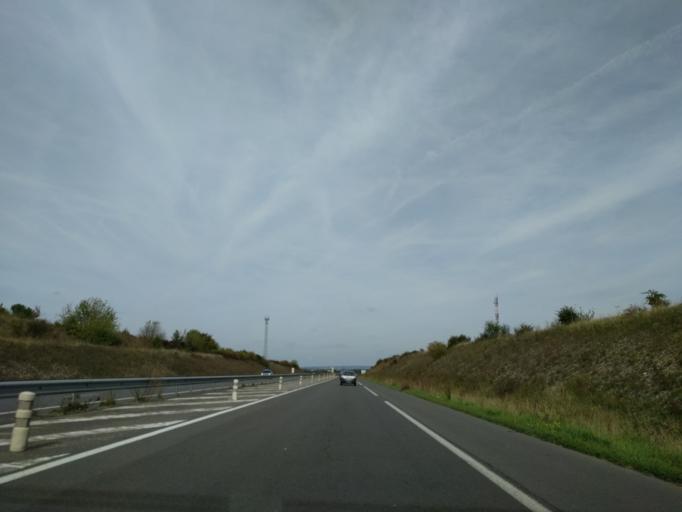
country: FR
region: Centre
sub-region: Departement du Cher
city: Bourges
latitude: 47.0780
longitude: 2.4406
